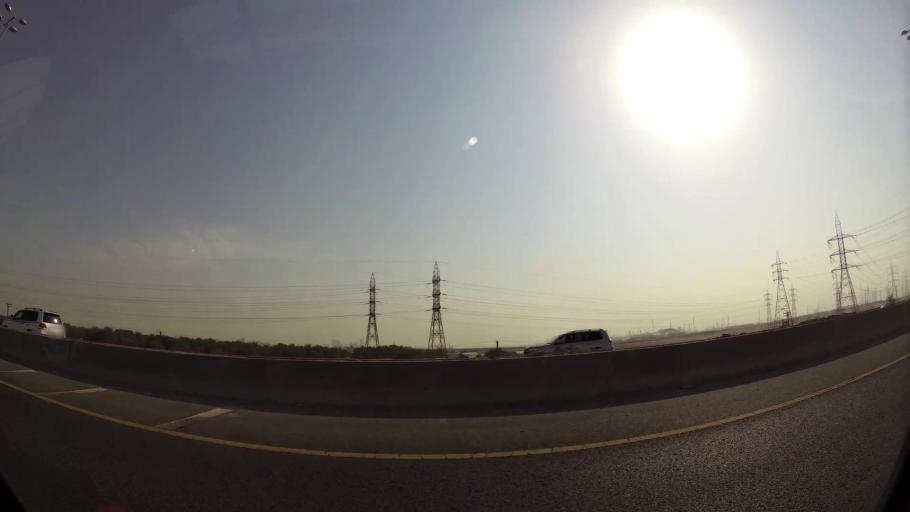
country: KW
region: Al Ahmadi
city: Al Ahmadi
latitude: 29.0729
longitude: 48.0995
